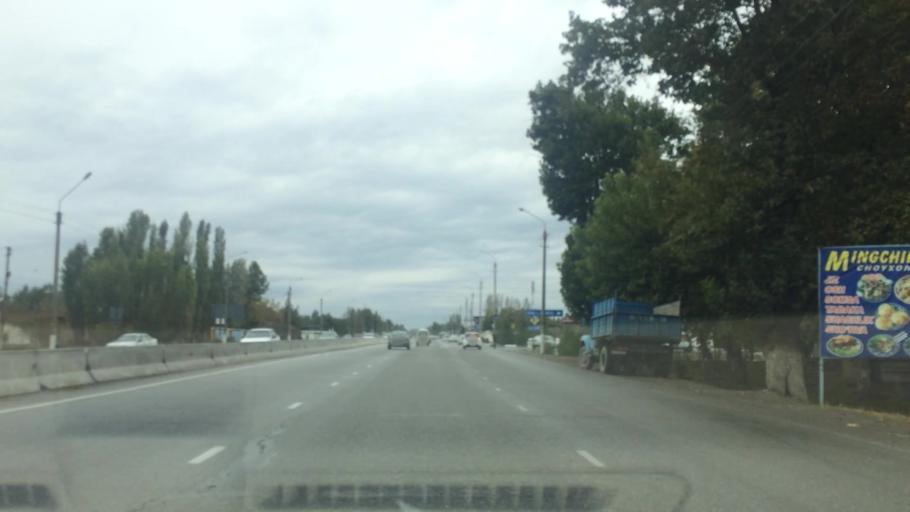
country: UZ
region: Jizzax
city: Jizzax
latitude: 40.0051
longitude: 67.5951
